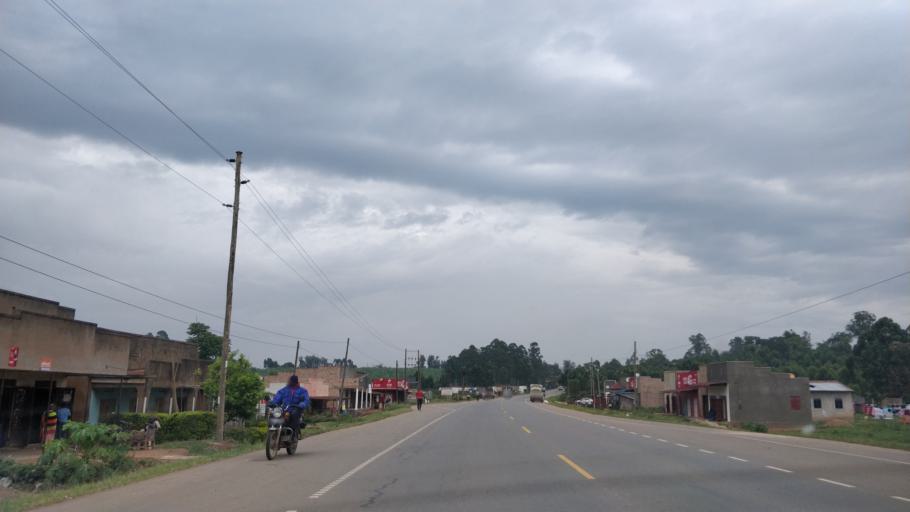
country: UG
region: Western Region
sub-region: Sheema District
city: Kibingo
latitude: -0.6597
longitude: 30.4583
